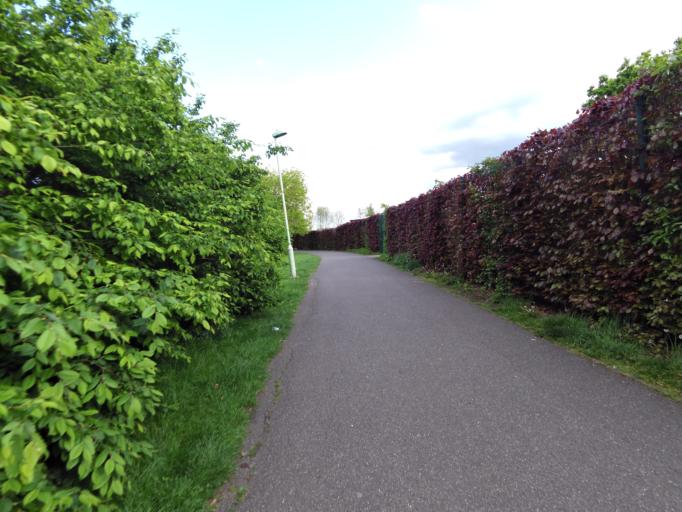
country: GB
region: England
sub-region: Suffolk
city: Stowmarket
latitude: 52.1942
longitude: 0.9793
